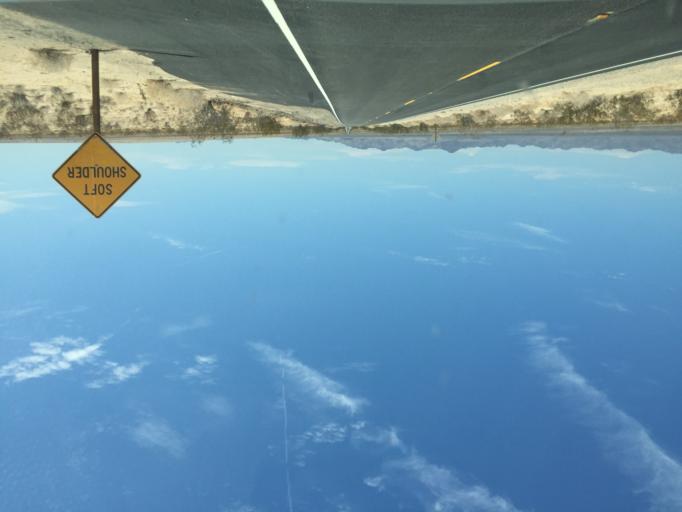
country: US
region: California
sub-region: Riverside County
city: Mesa Verde
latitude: 34.0996
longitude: -115.0055
